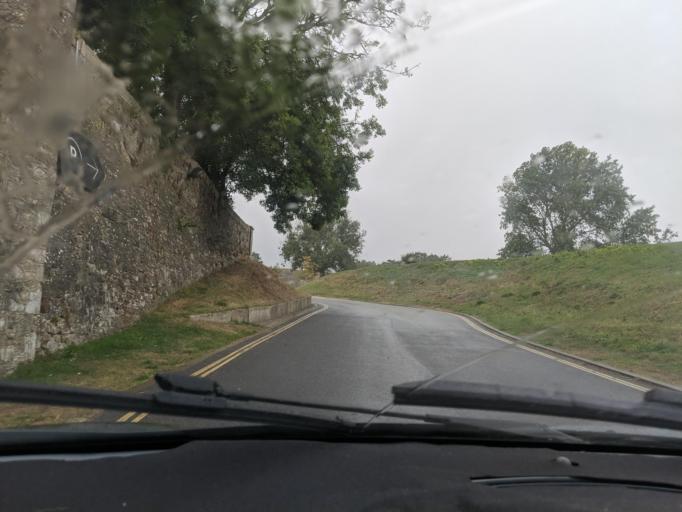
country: GB
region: England
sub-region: Cornwall
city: Millbrook
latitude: 50.3613
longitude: -4.1625
